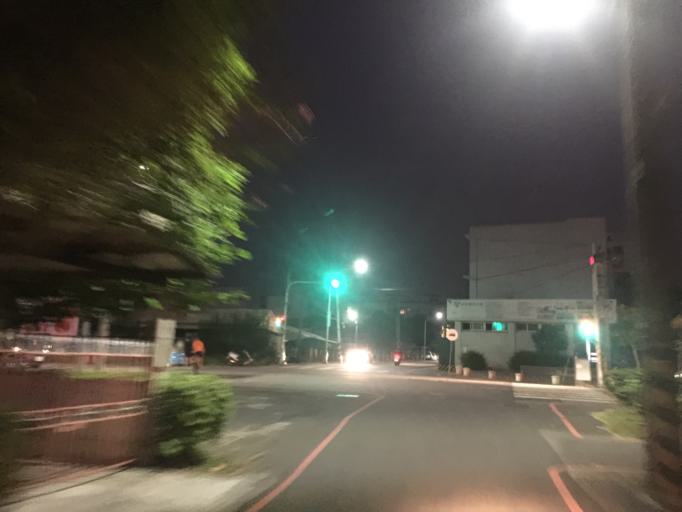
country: TW
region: Taiwan
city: Xinying
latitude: 23.3124
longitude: 120.3230
